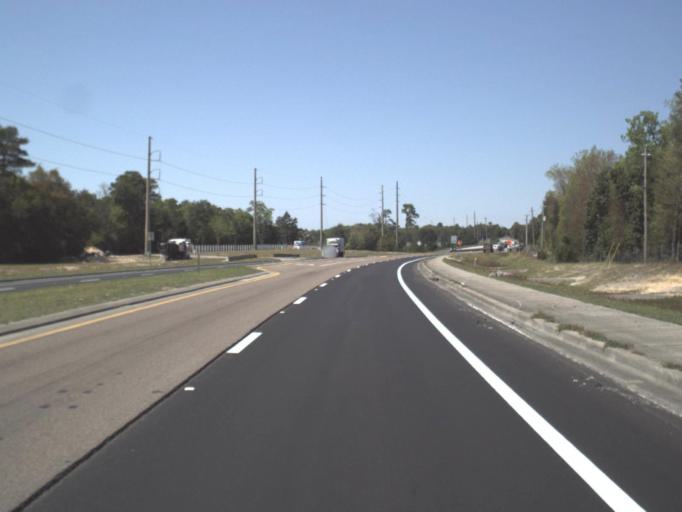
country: US
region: Florida
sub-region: Okaloosa County
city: Niceville
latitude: 30.4998
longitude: -86.4374
